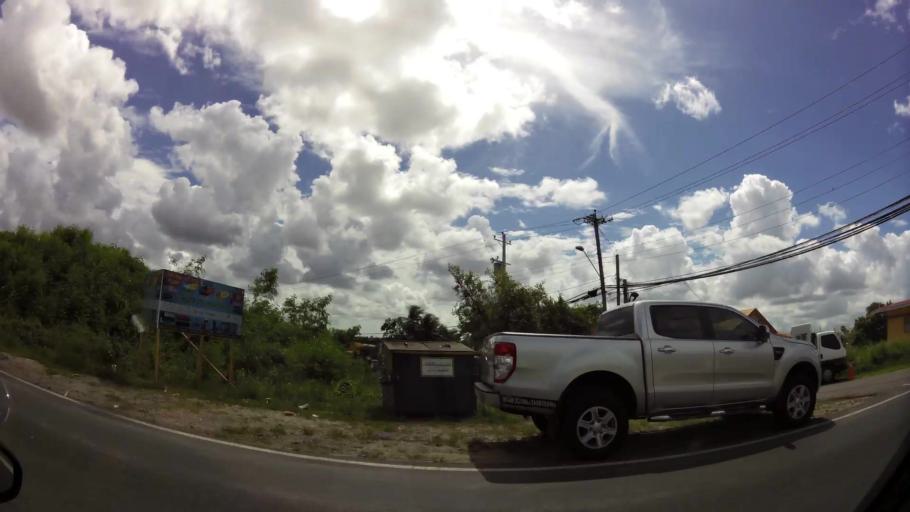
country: TT
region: City of San Fernando
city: Marabella
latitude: 10.2998
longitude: -61.4498
